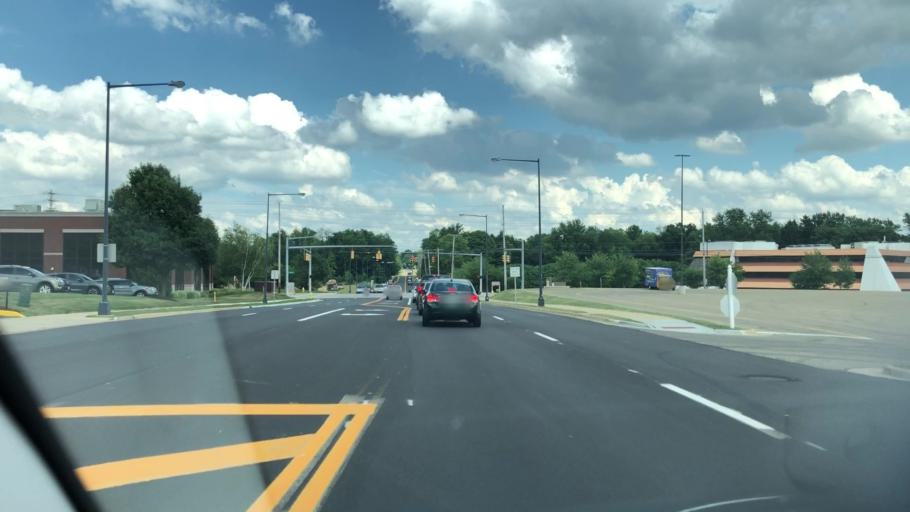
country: US
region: Ohio
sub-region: Summit County
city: Fairlawn
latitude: 41.1359
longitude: -81.6160
